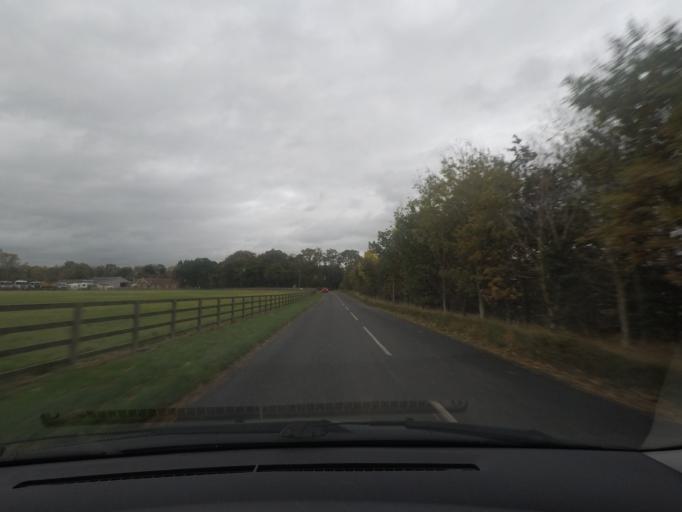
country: GB
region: England
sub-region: City of York
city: Wigginton
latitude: 54.0614
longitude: -1.0924
